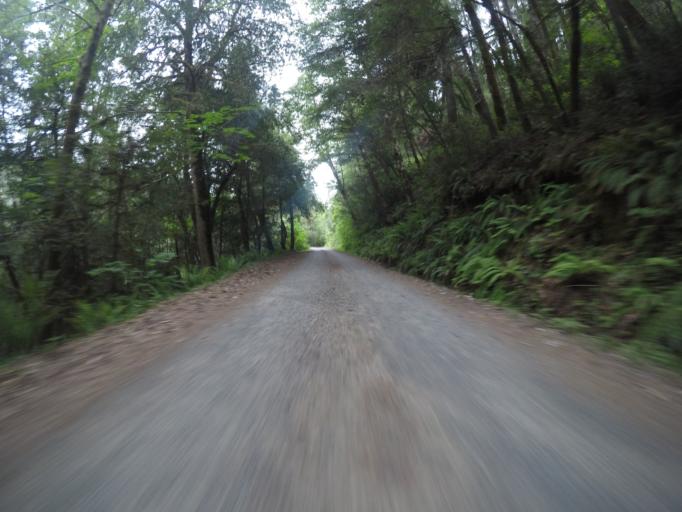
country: US
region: California
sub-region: Del Norte County
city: Bertsch-Oceanview
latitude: 41.7225
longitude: -123.8973
